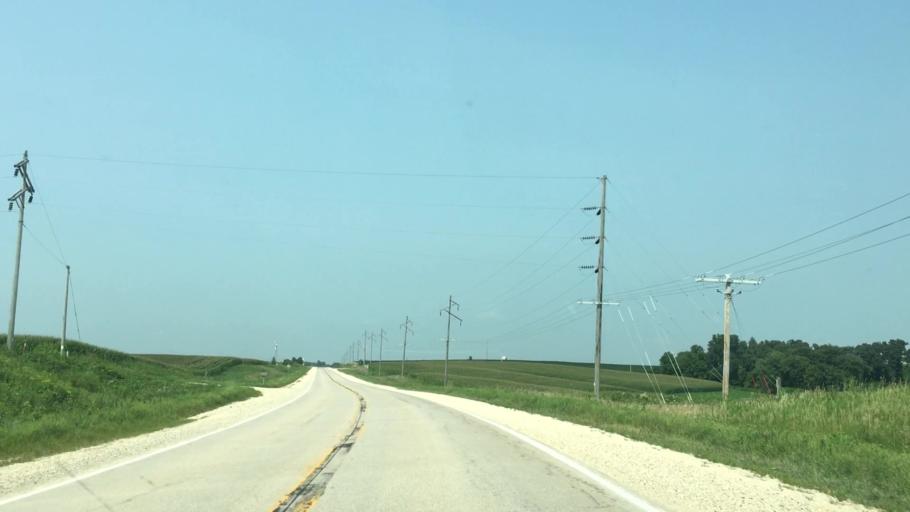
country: US
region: Iowa
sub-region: Winneshiek County
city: Decorah
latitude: 43.1432
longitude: -91.8643
